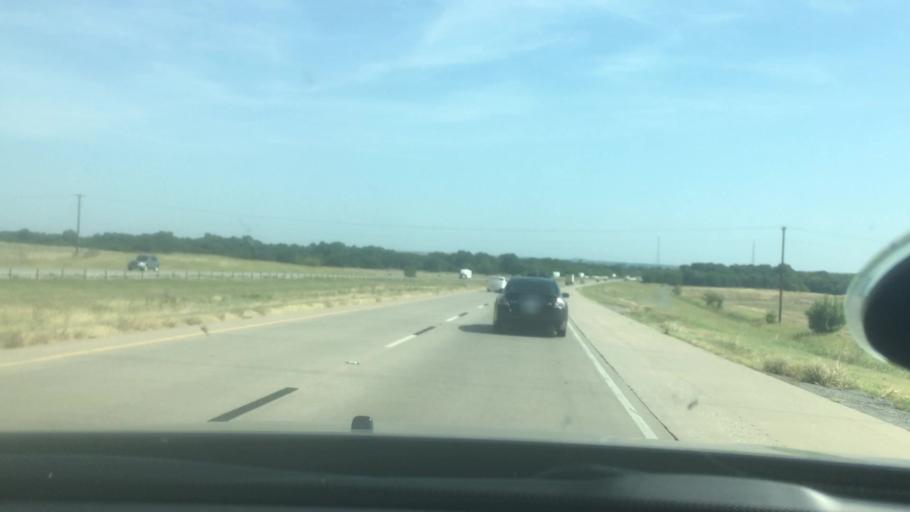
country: US
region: Oklahoma
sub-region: Carter County
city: Ardmore
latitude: 34.2550
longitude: -97.1648
